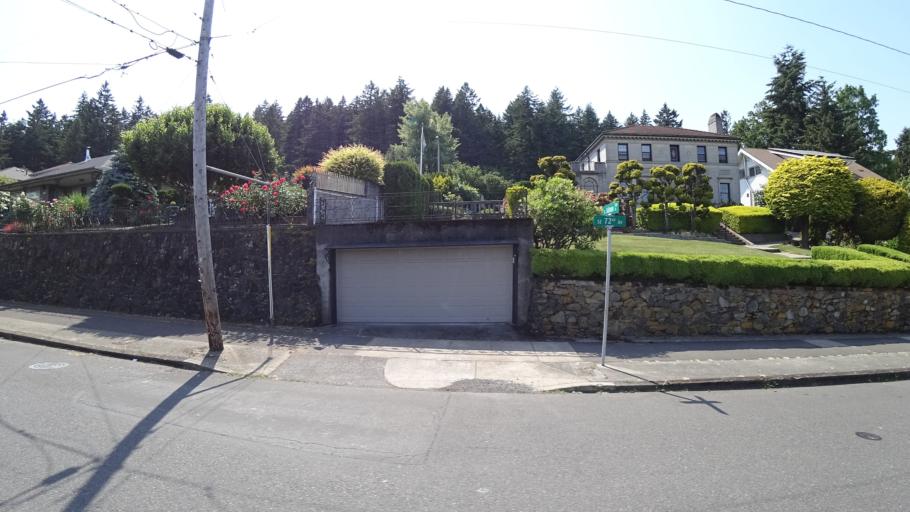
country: US
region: Oregon
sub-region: Multnomah County
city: Lents
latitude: 45.5144
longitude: -122.5890
